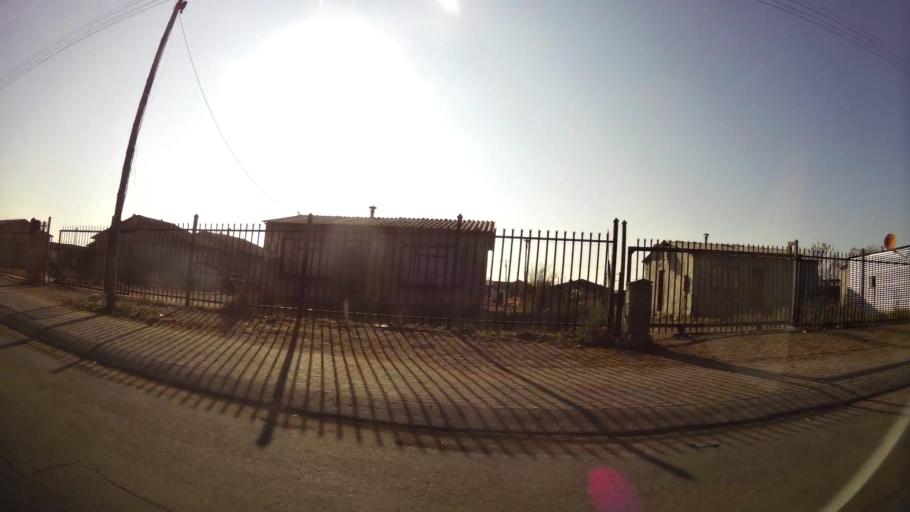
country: ZA
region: Orange Free State
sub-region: Mangaung Metropolitan Municipality
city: Bloemfontein
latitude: -29.1535
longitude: 26.2530
